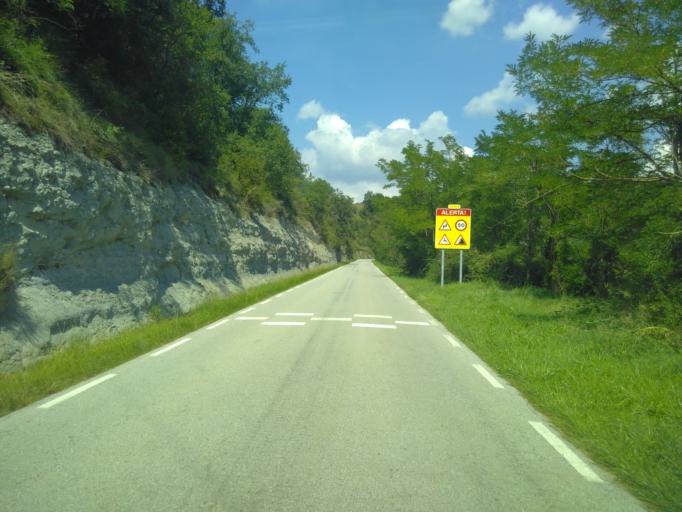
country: ES
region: Catalonia
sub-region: Provincia de Barcelona
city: Montesquiu
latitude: 42.1028
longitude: 2.2232
